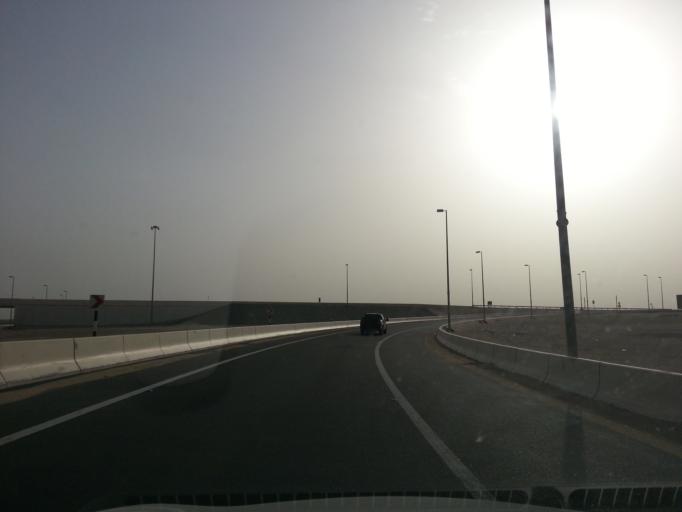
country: AE
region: Dubai
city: Dubai
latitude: 24.7935
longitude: 55.0786
